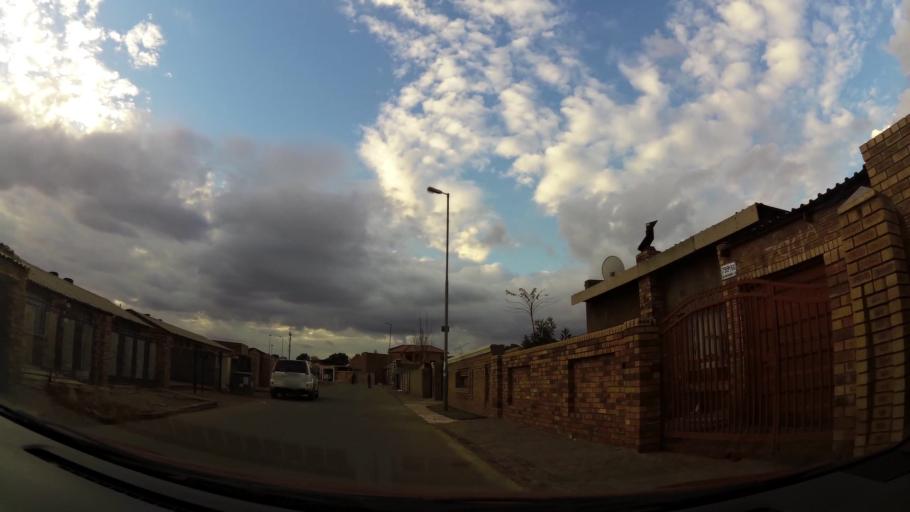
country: ZA
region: Gauteng
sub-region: City of Johannesburg Metropolitan Municipality
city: Soweto
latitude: -26.2465
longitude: 27.8310
